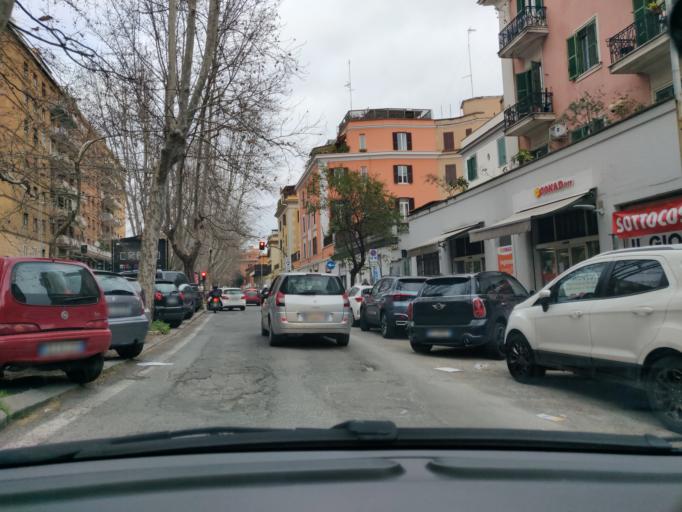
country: VA
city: Vatican City
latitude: 41.9050
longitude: 12.4473
